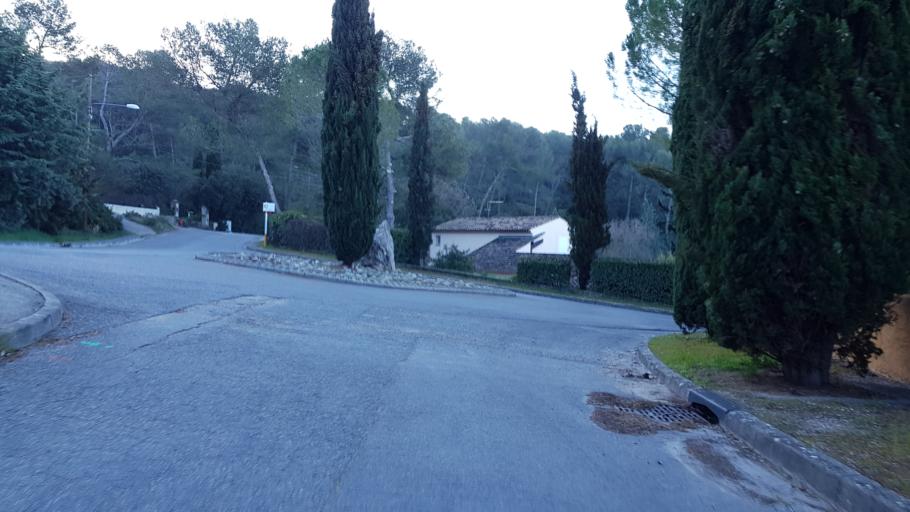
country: FR
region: Provence-Alpes-Cote d'Azur
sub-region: Departement des Bouches-du-Rhone
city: Bouc-Bel-Air
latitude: 43.4837
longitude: 5.4267
